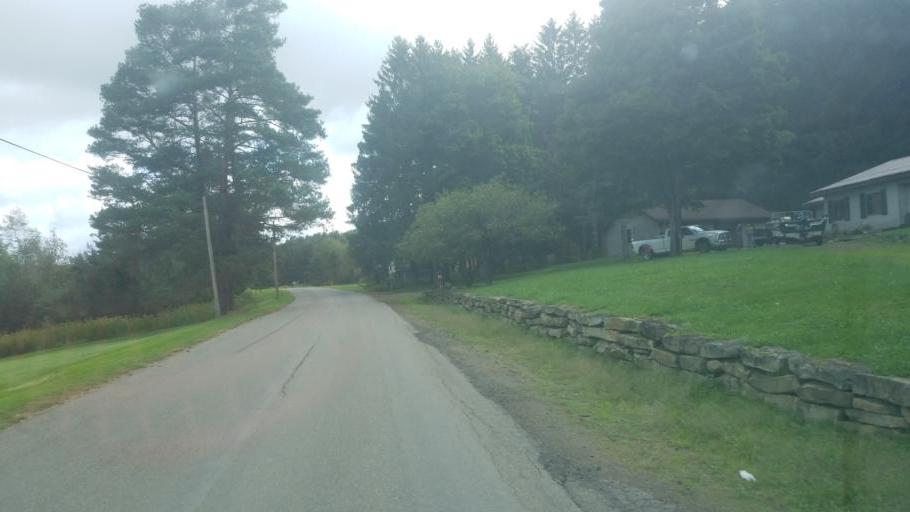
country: US
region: New York
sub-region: Cattaraugus County
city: Weston Mills
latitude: 42.1189
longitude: -78.3105
